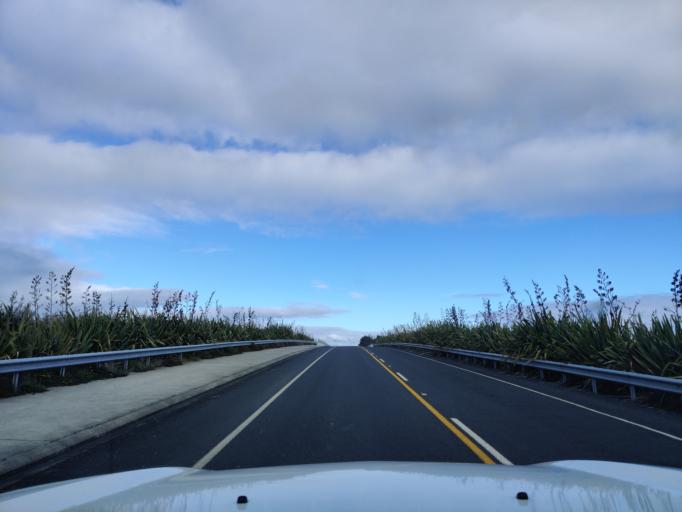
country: NZ
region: Waikato
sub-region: Waipa District
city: Cambridge
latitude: -37.8671
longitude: 175.4390
